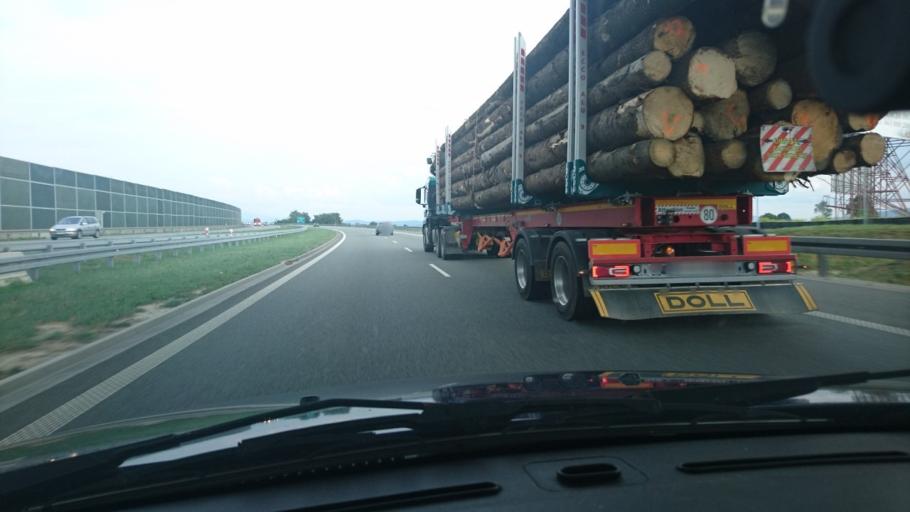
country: PL
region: Silesian Voivodeship
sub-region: Powiat bielski
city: Rybarzowice
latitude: 49.7439
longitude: 19.0920
